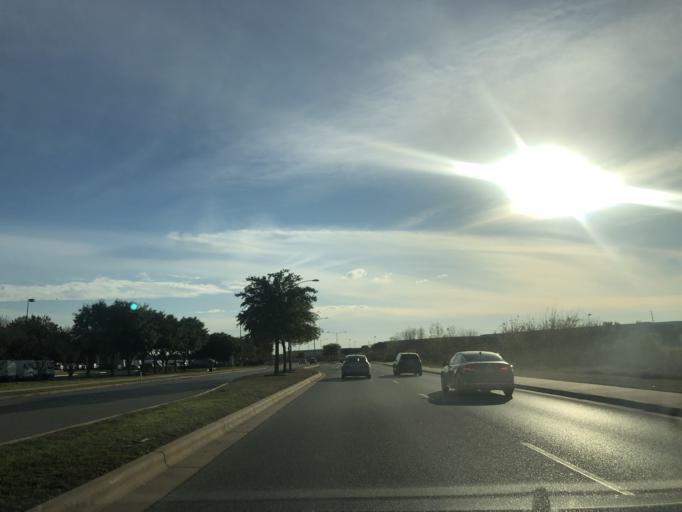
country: US
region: Texas
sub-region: Travis County
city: Wells Branch
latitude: 30.4183
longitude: -97.6616
